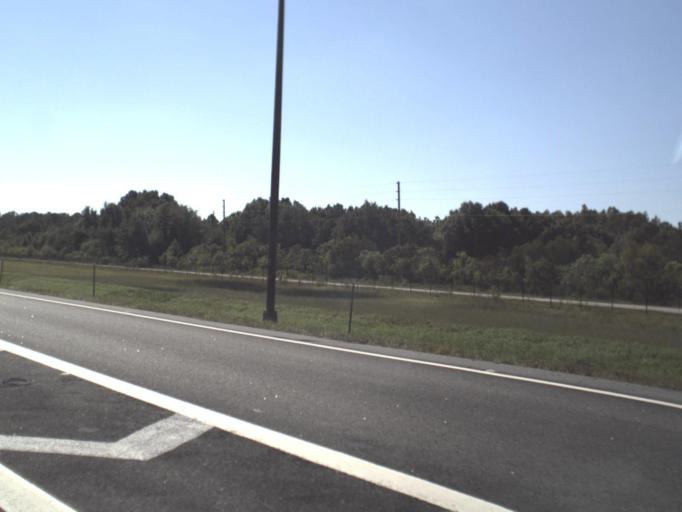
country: US
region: Florida
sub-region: Pasco County
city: Odessa
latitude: 28.1950
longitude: -82.5466
